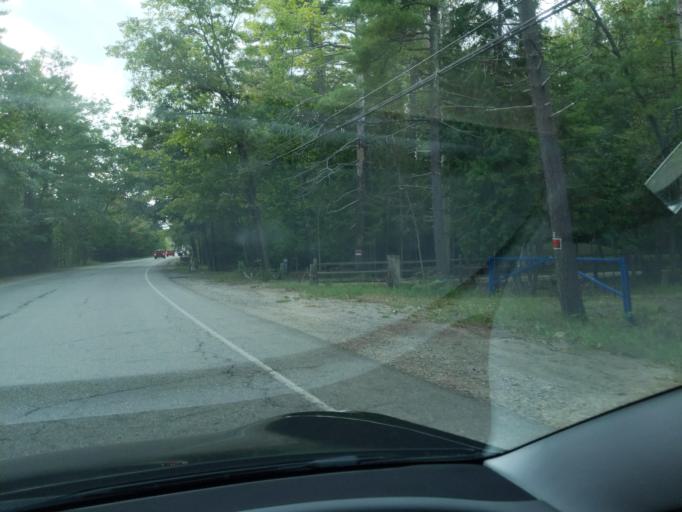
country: US
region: Michigan
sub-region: Kalkaska County
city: Rapid City
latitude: 44.8521
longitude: -85.3167
